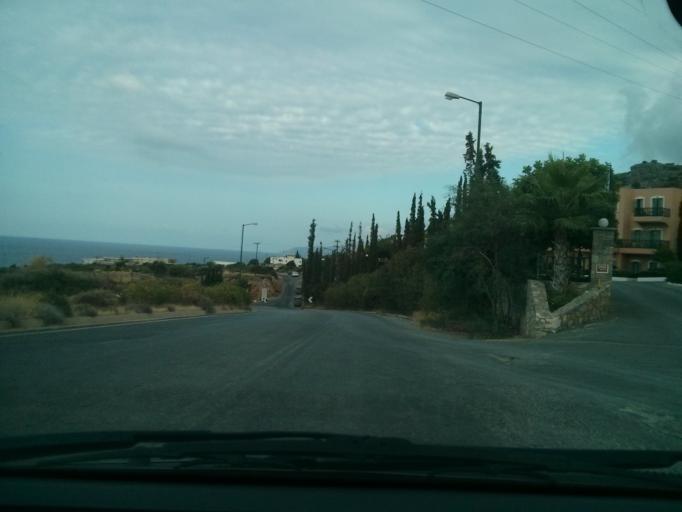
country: GR
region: Crete
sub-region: Nomos Irakleiou
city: Stalis
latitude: 35.3018
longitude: 25.4108
